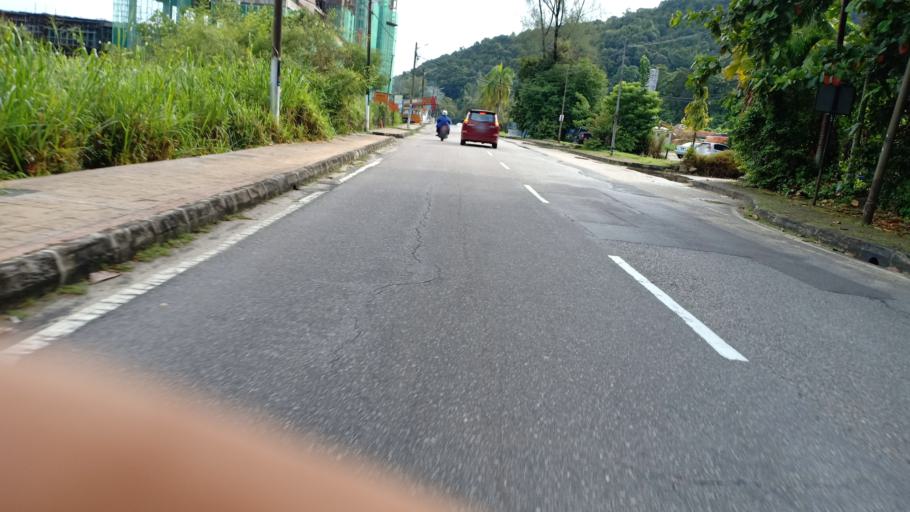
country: MY
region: Penang
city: Tanjung Tokong
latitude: 5.4604
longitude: 100.2184
